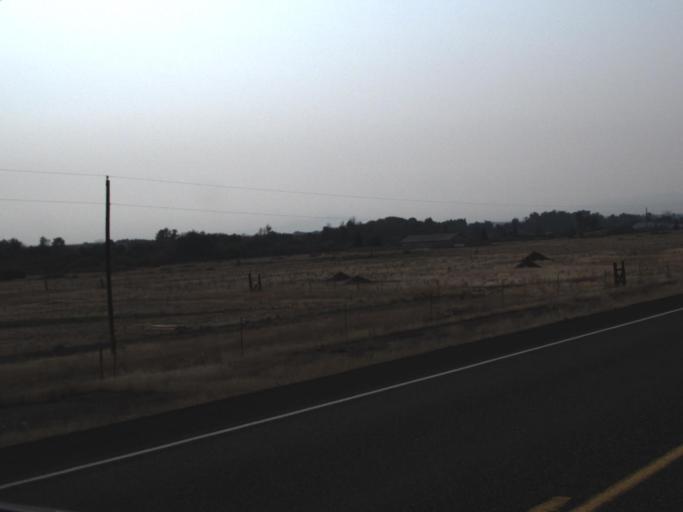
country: US
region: Washington
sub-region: Kittitas County
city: Ellensburg
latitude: 47.0639
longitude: -120.6225
